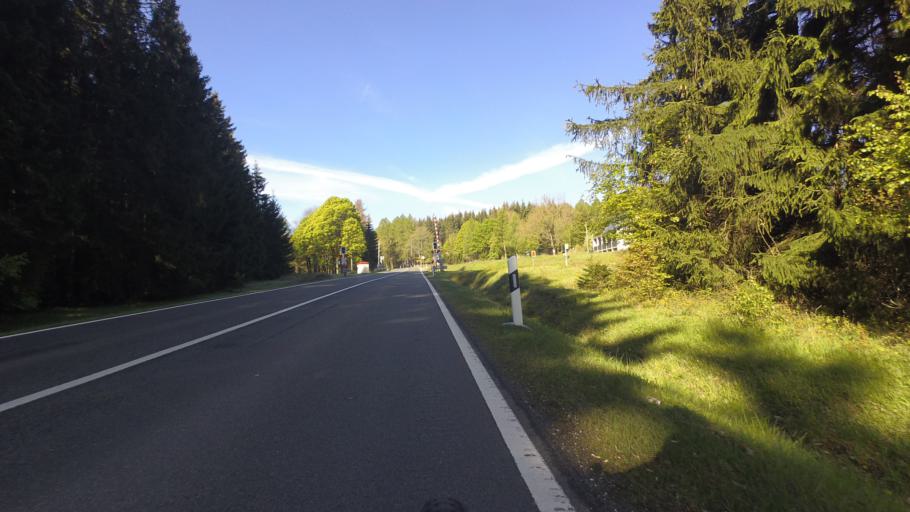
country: DE
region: Saxony-Anhalt
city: Darlingerode
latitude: 51.7814
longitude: 10.7377
